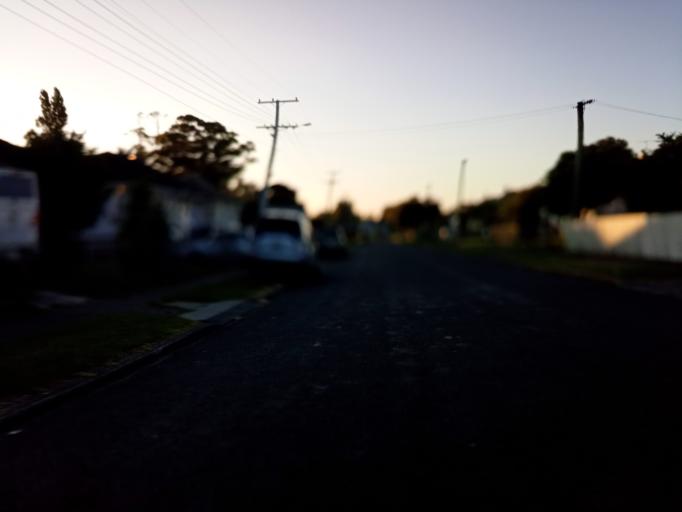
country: NZ
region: Gisborne
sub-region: Gisborne District
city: Gisborne
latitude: -38.6483
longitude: 178.0097
